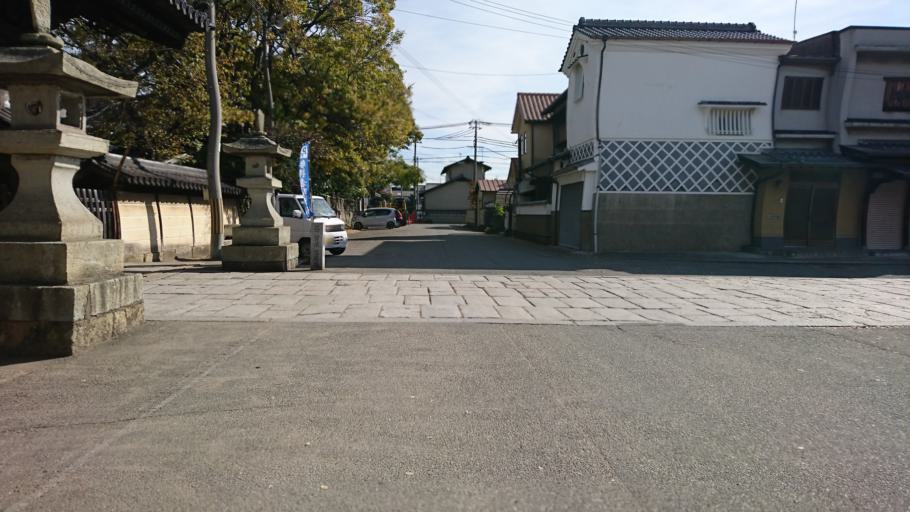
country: JP
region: Hyogo
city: Kakogawacho-honmachi
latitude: 34.7432
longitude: 134.8032
